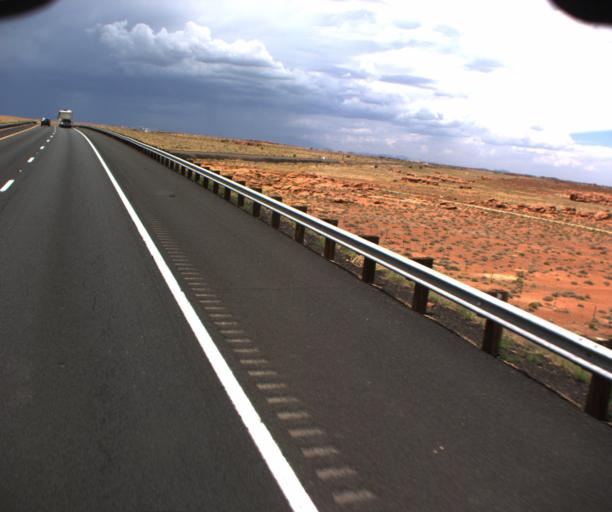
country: US
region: Arizona
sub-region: Coconino County
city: LeChee
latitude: 35.1002
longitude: -110.9712
